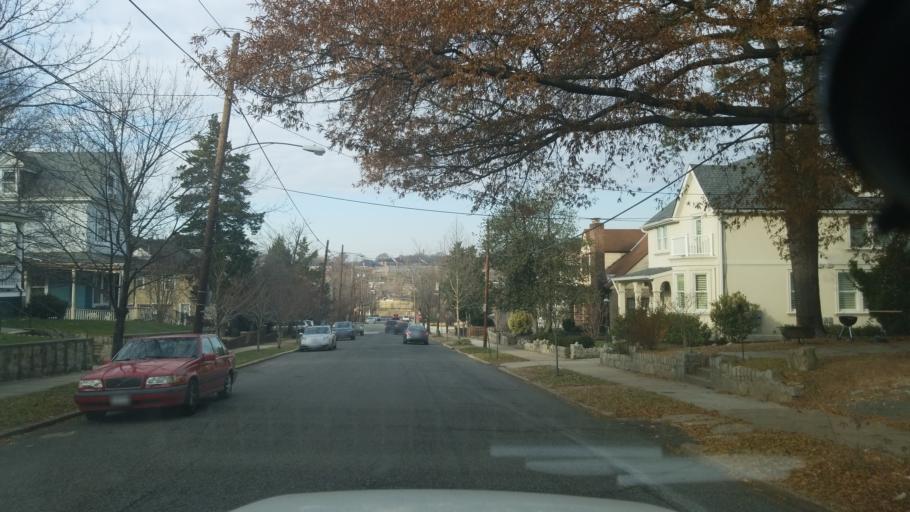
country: US
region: Maryland
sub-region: Prince George's County
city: Mount Rainier
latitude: 38.9373
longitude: -76.9891
